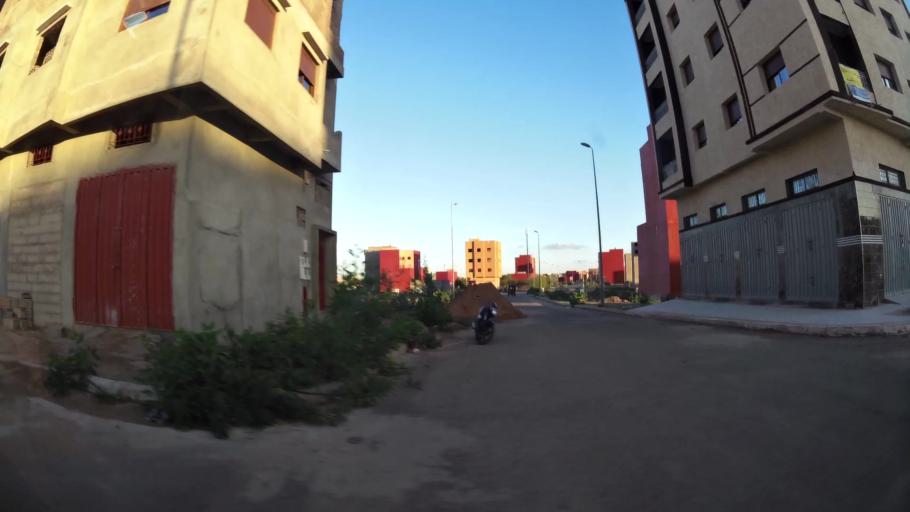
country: MA
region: Marrakech-Tensift-Al Haouz
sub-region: Kelaa-Des-Sraghna
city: Sidi Abdallah
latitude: 32.2370
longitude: -7.9428
